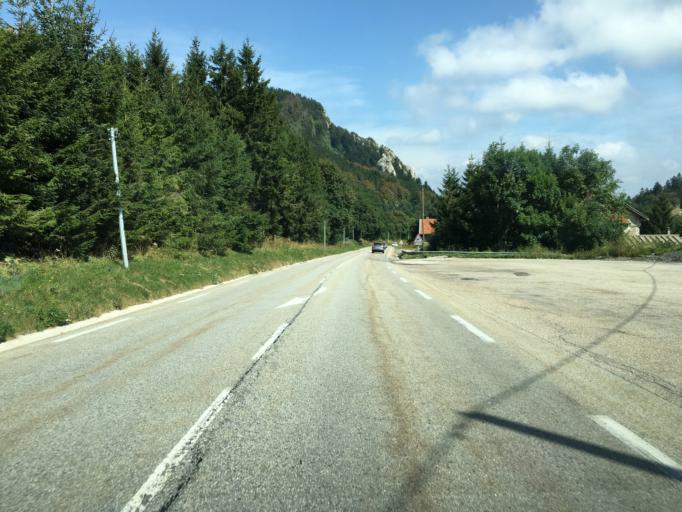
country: FR
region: Rhone-Alpes
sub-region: Departement de l'Isere
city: Mens
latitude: 44.7261
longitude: 5.6778
